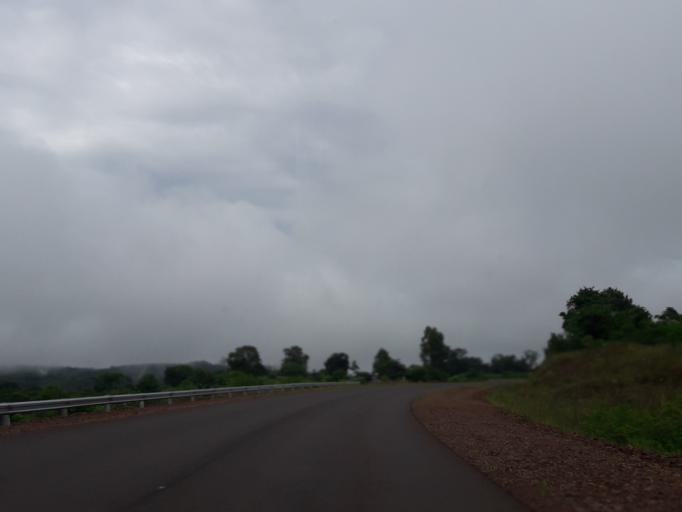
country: AR
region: Misiones
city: Bernardo de Irigoyen
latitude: -26.4201
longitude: -53.8267
